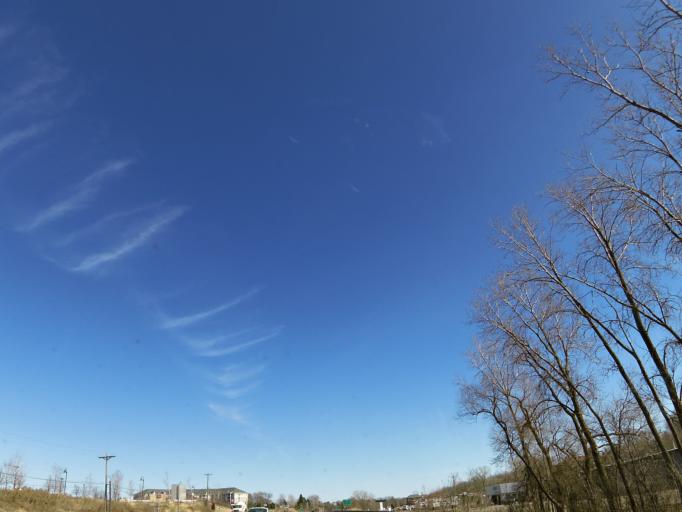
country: US
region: Minnesota
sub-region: Hennepin County
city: Medina
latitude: 45.0441
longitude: -93.5318
